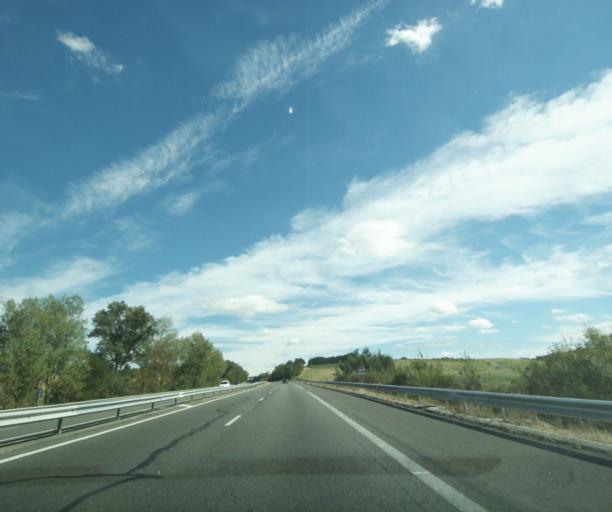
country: FR
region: Midi-Pyrenees
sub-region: Departement du Tarn-et-Garonne
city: Lamagistere
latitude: 44.0711
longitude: 0.8142
